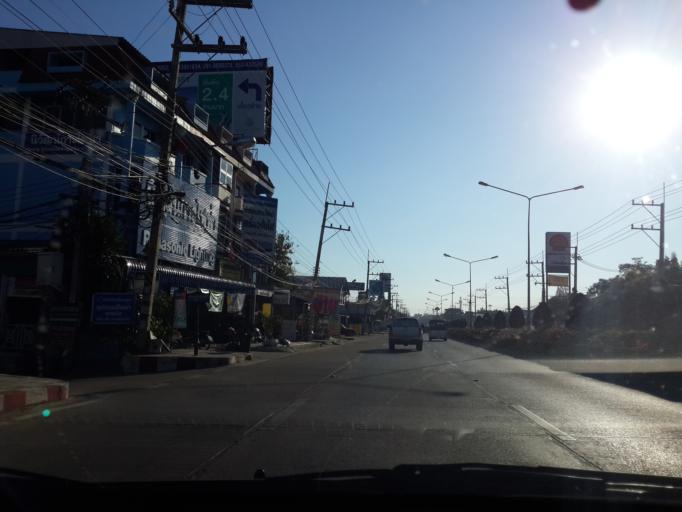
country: TH
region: Chiang Mai
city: Hang Dong
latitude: 18.6962
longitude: 98.9273
